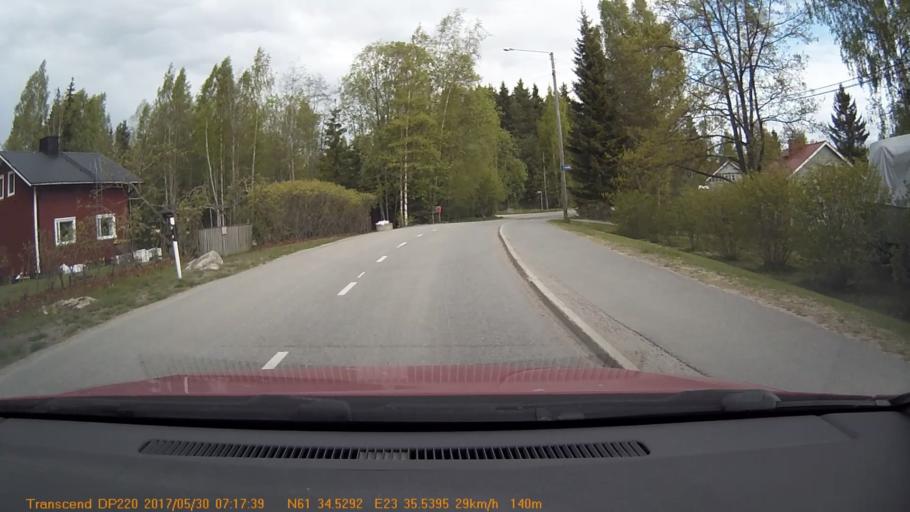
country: FI
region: Pirkanmaa
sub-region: Tampere
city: Yloejaervi
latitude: 61.5754
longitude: 23.5923
